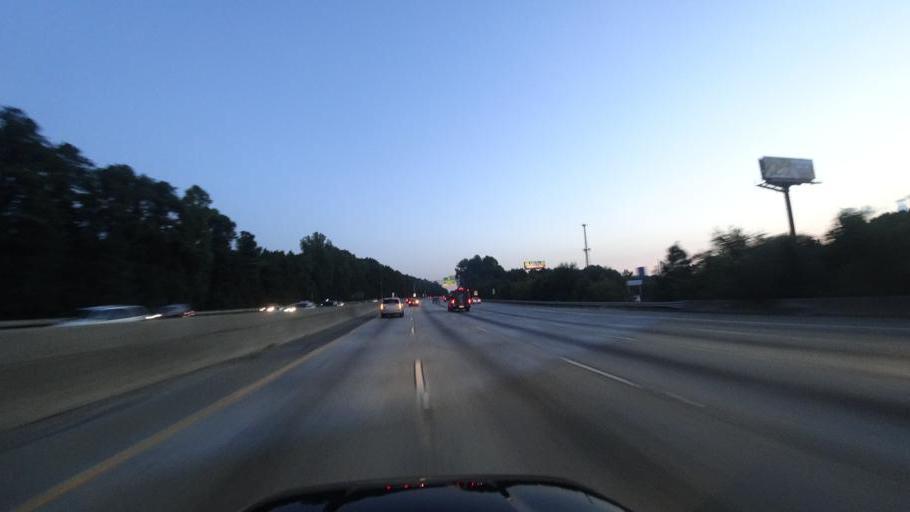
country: US
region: Georgia
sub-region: DeKalb County
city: Clarkston
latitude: 33.8388
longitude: -84.2482
